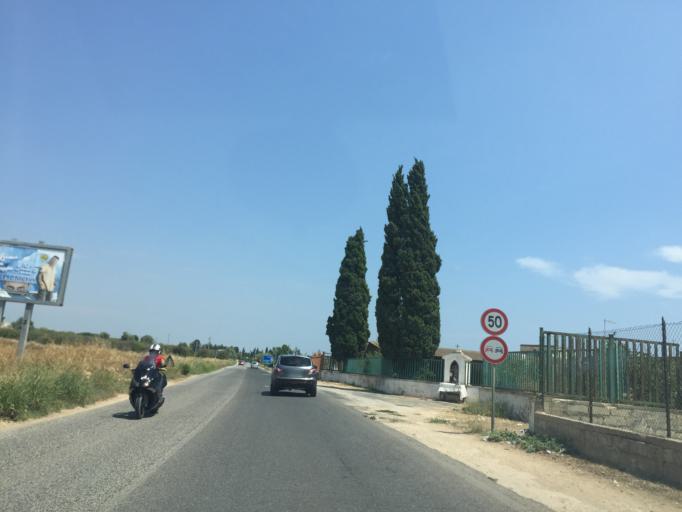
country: IT
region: Sicily
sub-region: Provincia di Siracusa
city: Avola
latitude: 36.9261
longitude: 15.1608
